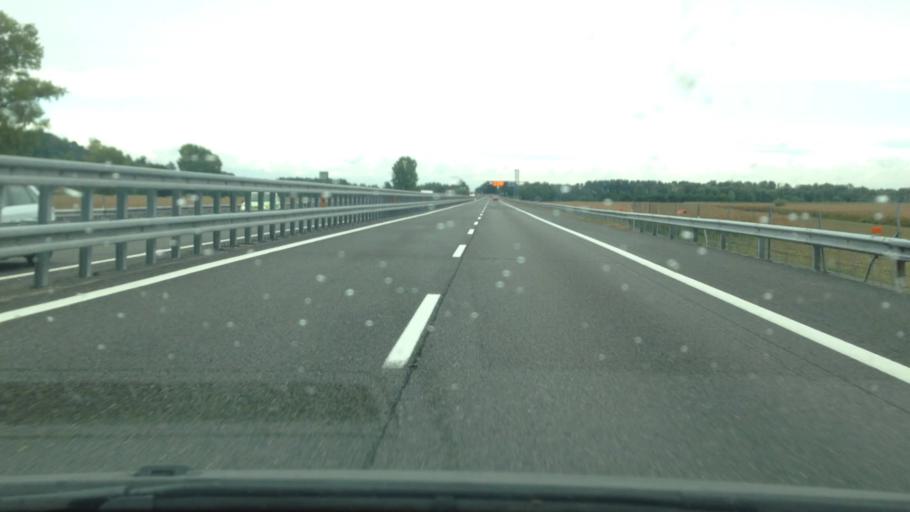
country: IT
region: Piedmont
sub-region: Provincia di Alessandria
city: Pietra Marazzi
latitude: 44.9379
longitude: 8.6533
